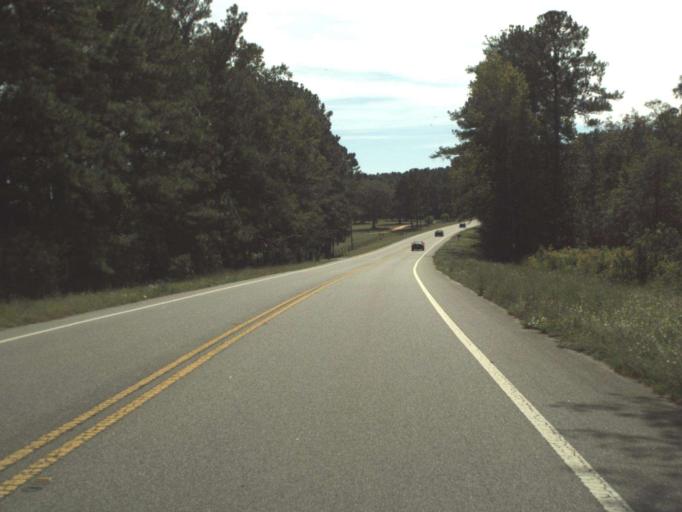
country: US
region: Florida
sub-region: Washington County
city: Chipley
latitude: 30.6097
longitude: -85.5938
